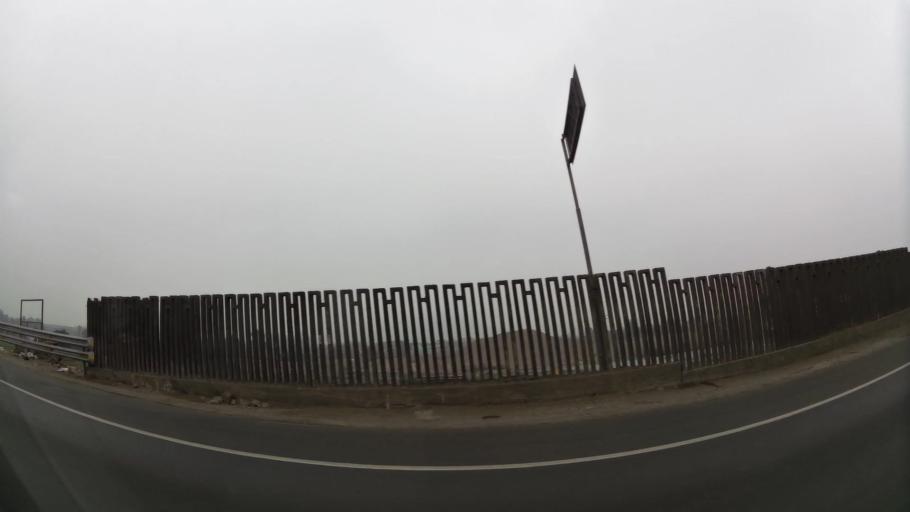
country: PE
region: Lima
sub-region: Lima
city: Santa Maria
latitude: -12.0169
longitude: -76.9083
